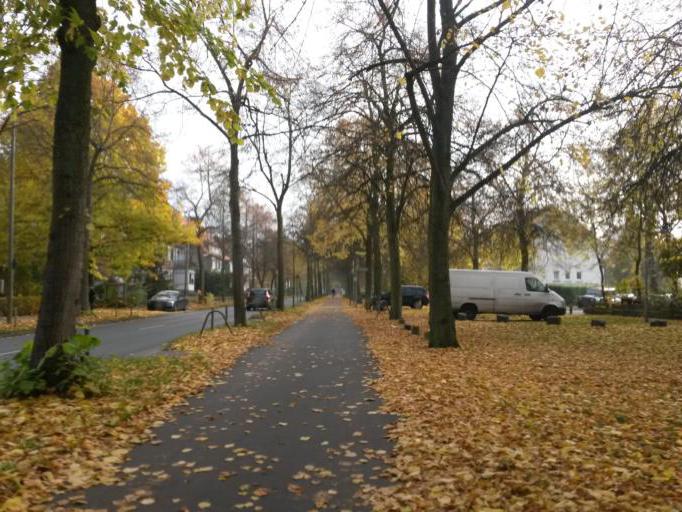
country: DE
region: Bremen
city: Bremen
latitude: 53.0883
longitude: 8.8435
